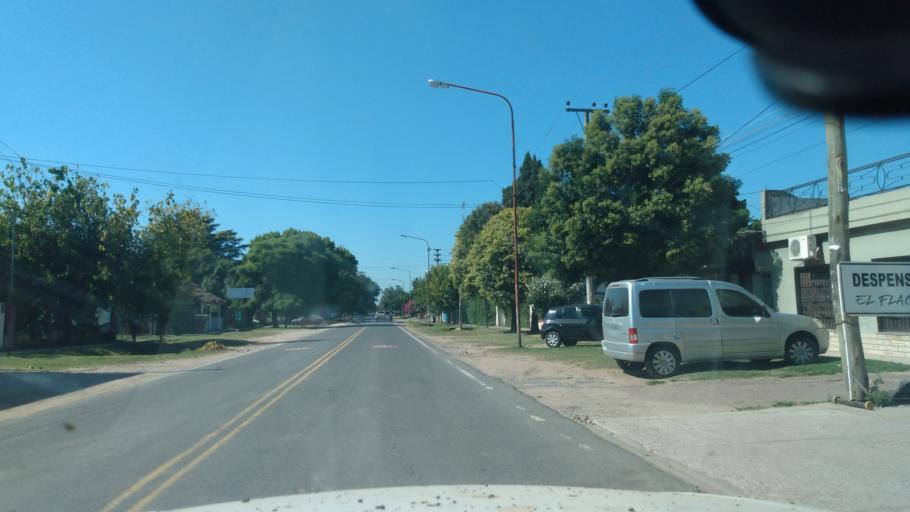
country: AR
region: Buenos Aires
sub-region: Partido de Lujan
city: Lujan
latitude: -34.4951
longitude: -59.0747
